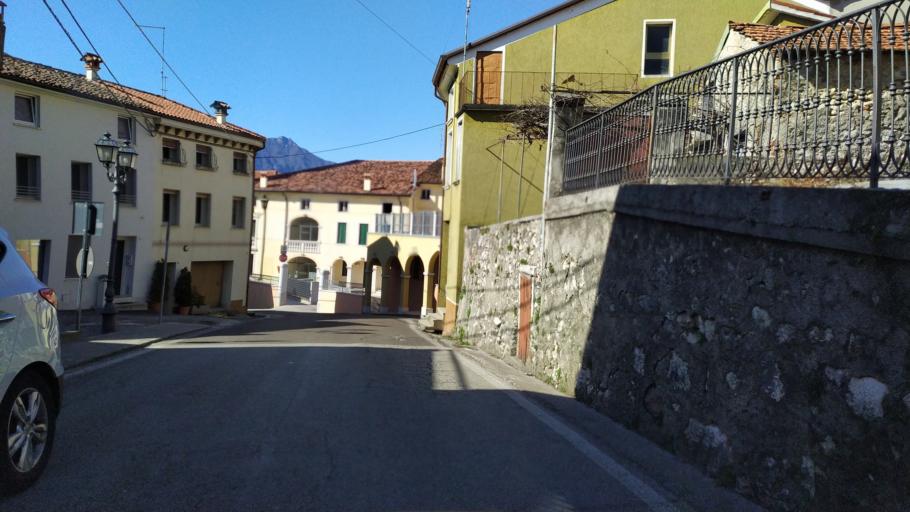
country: IT
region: Veneto
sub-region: Provincia di Vicenza
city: Caltrano
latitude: 45.7704
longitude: 11.4617
